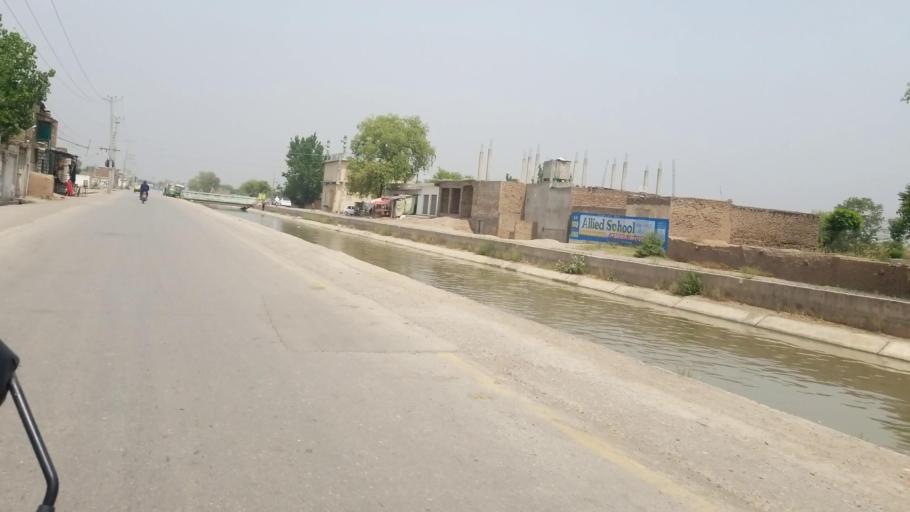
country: PK
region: Khyber Pakhtunkhwa
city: Peshawar
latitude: 33.9512
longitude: 71.5526
